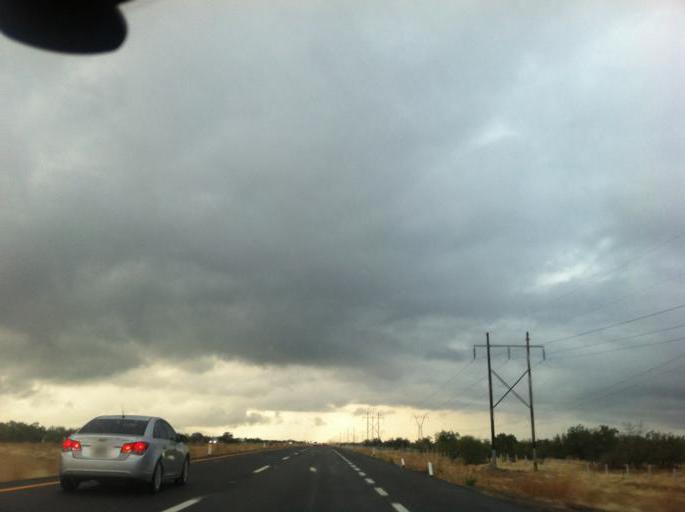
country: MX
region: Sonora
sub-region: Hermosillo
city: Estacion Zamora
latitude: 29.2583
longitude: -110.9405
